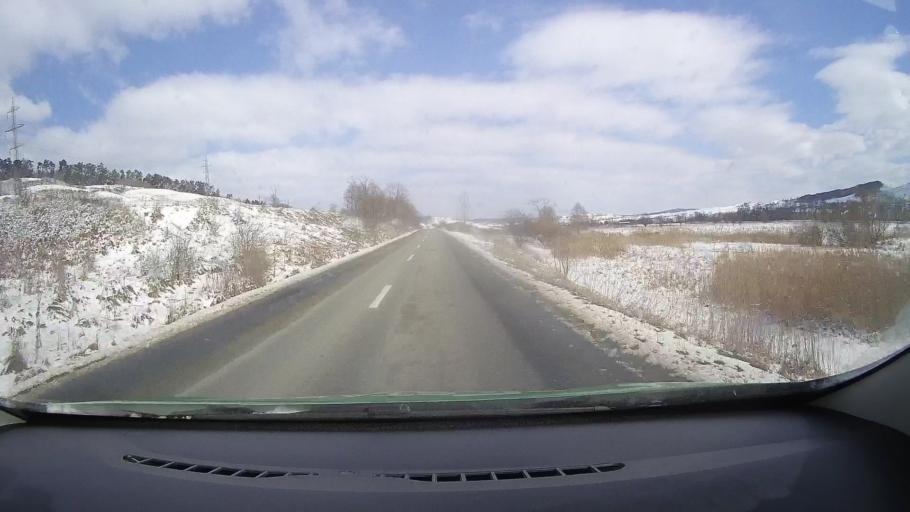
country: RO
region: Sibiu
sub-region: Comuna Barghis
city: Barghis
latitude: 45.9626
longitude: 24.5690
